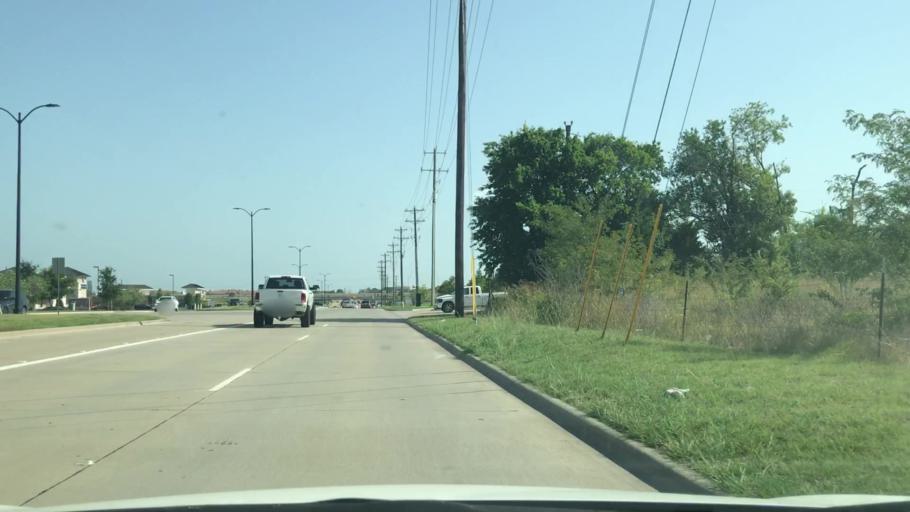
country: US
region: Texas
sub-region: Collin County
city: Frisco
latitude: 33.1235
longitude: -96.7509
